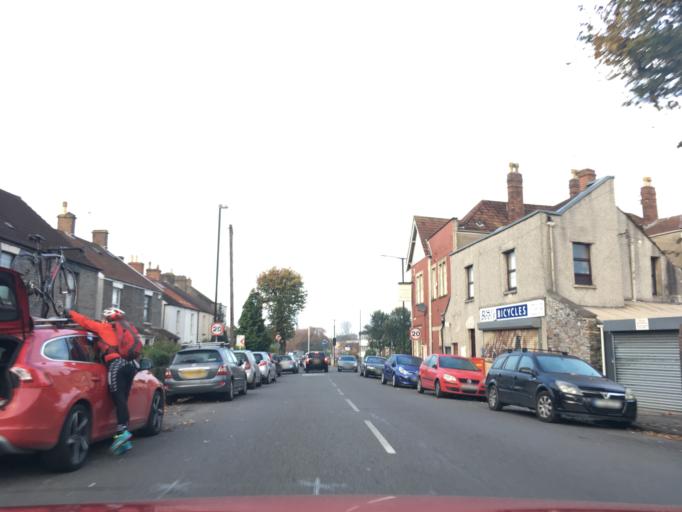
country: GB
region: England
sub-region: South Gloucestershire
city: Mangotsfield
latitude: 51.4817
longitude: -2.5226
